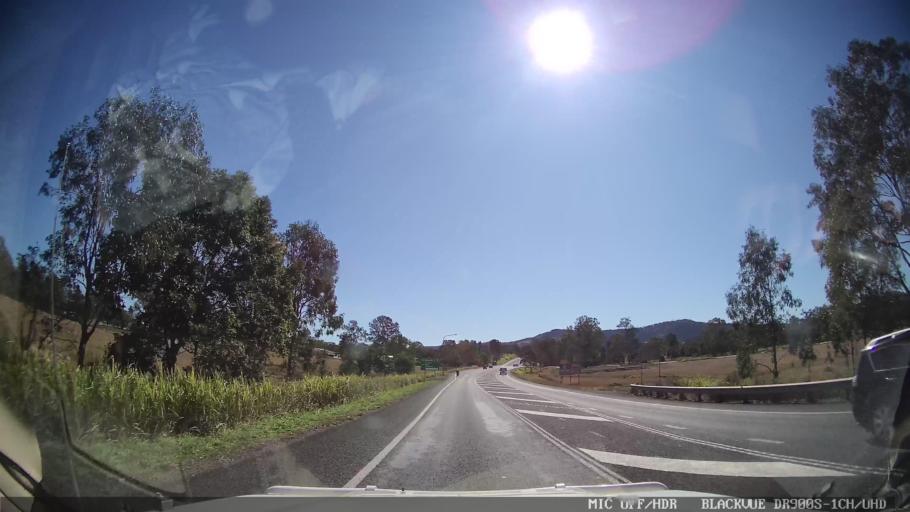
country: AU
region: Queensland
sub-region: Gympie Regional Council
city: Gympie
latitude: -25.9976
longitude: 152.5663
